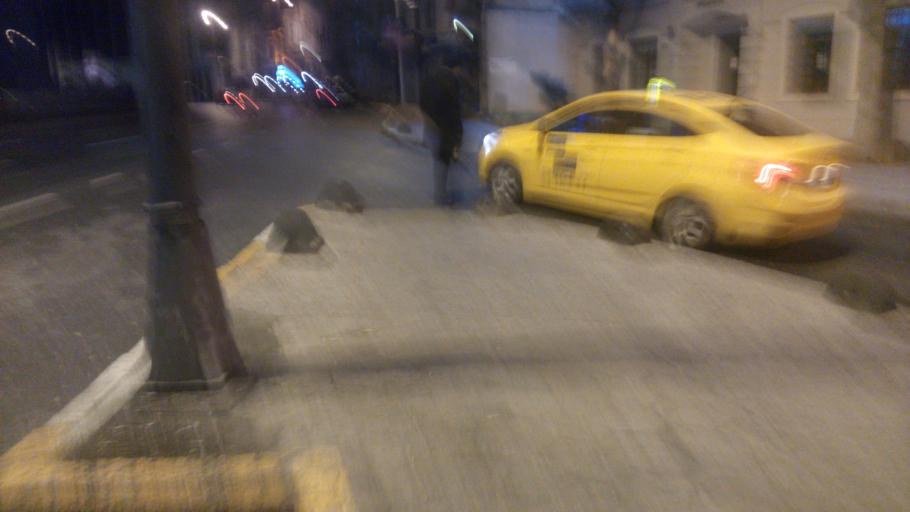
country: TR
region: Istanbul
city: Eminoenue
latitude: 41.0365
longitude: 28.9756
